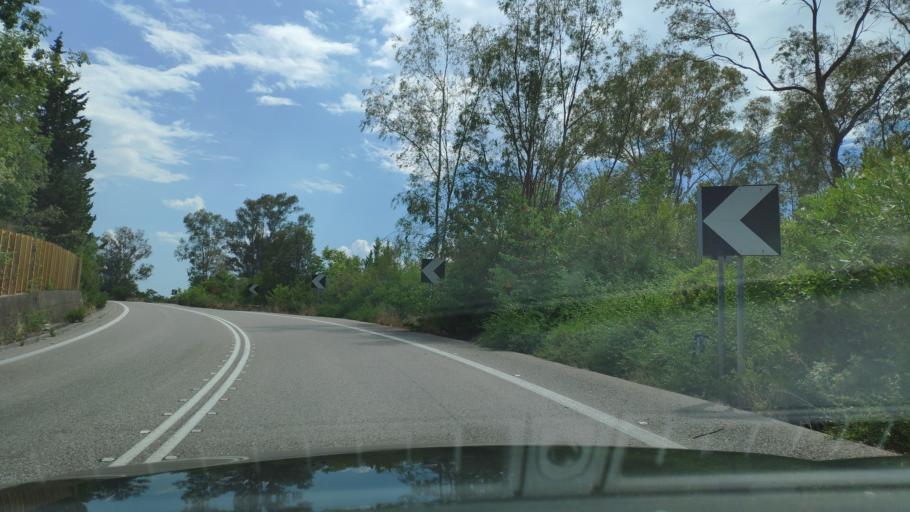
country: GR
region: West Greece
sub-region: Nomos Aitolias kai Akarnanias
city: Menidi
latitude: 39.0304
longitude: 21.1253
